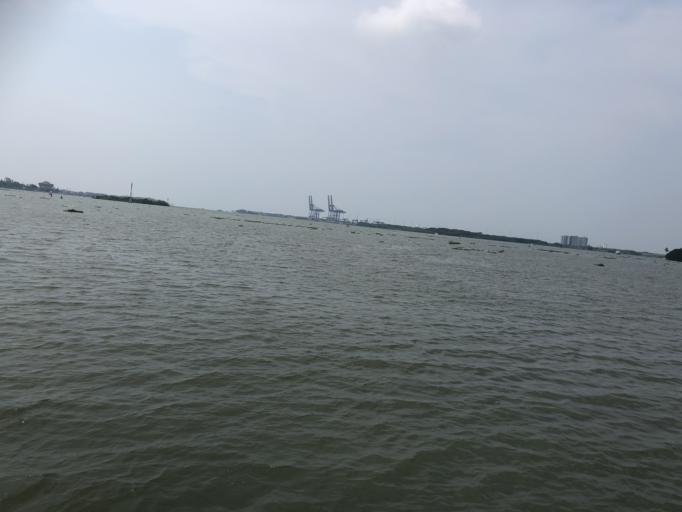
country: IN
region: Kerala
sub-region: Ernakulam
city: Cochin
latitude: 9.9790
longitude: 76.2746
